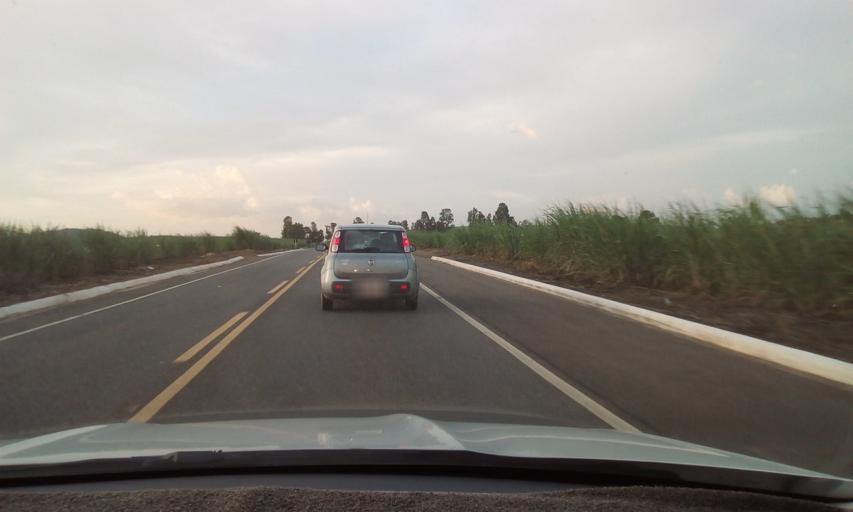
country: BR
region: Pernambuco
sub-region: Vicencia
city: Vicencia
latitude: -7.6055
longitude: -35.2404
